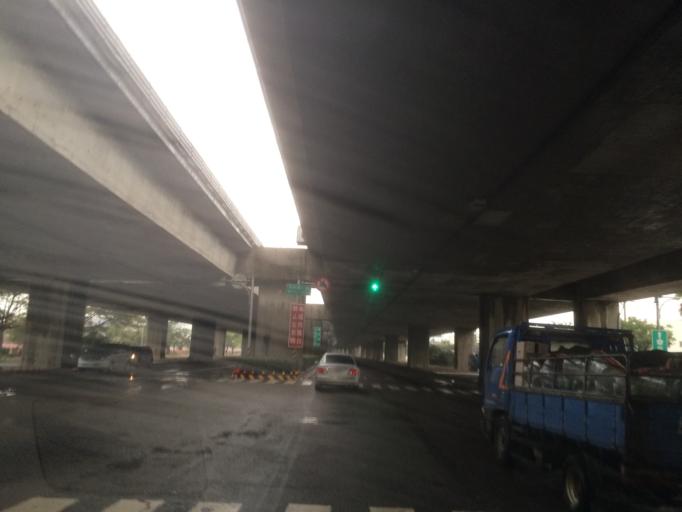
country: TW
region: Taiwan
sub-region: Taichung City
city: Taichung
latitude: 24.1599
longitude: 120.6271
